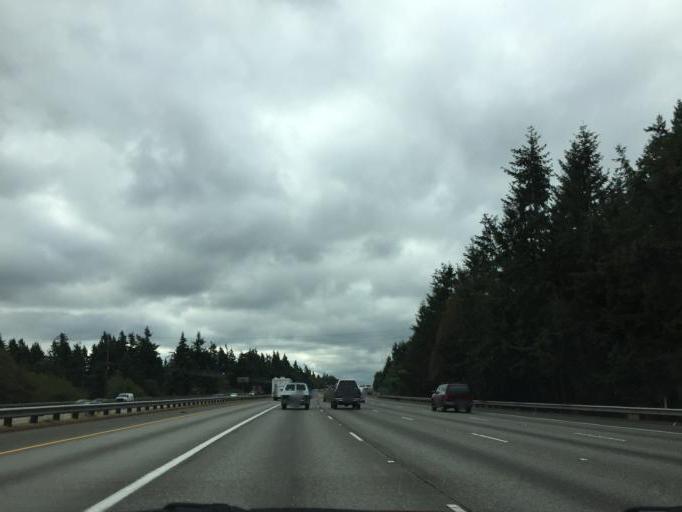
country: US
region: Washington
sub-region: King County
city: Lakeland North
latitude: 47.3449
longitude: -122.2930
